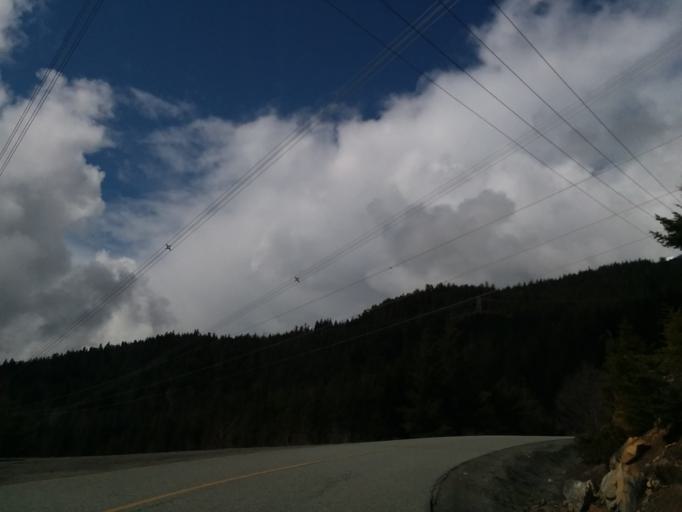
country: CA
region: British Columbia
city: Whistler
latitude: 50.1032
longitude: -122.9951
